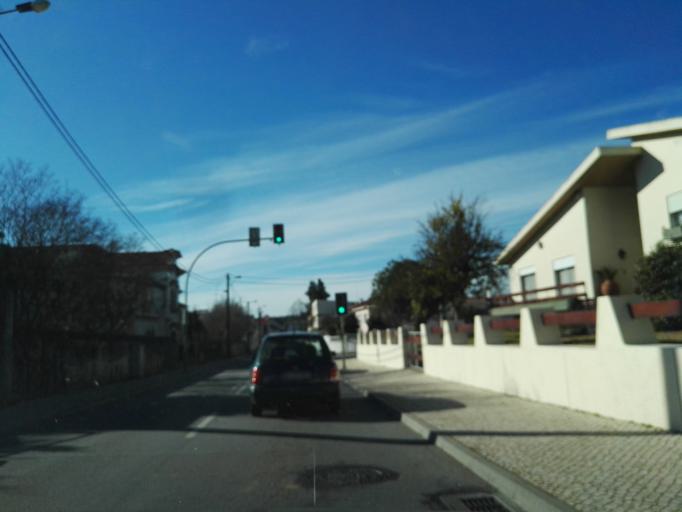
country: PT
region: Santarem
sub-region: Macao
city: Macao
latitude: 39.4640
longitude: -8.0408
